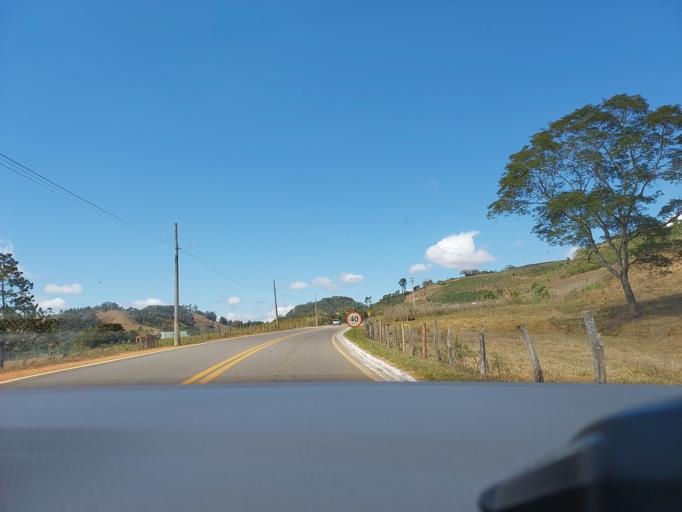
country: BR
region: Minas Gerais
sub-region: Mirai
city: Mirai
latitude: -21.0091
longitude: -42.5491
